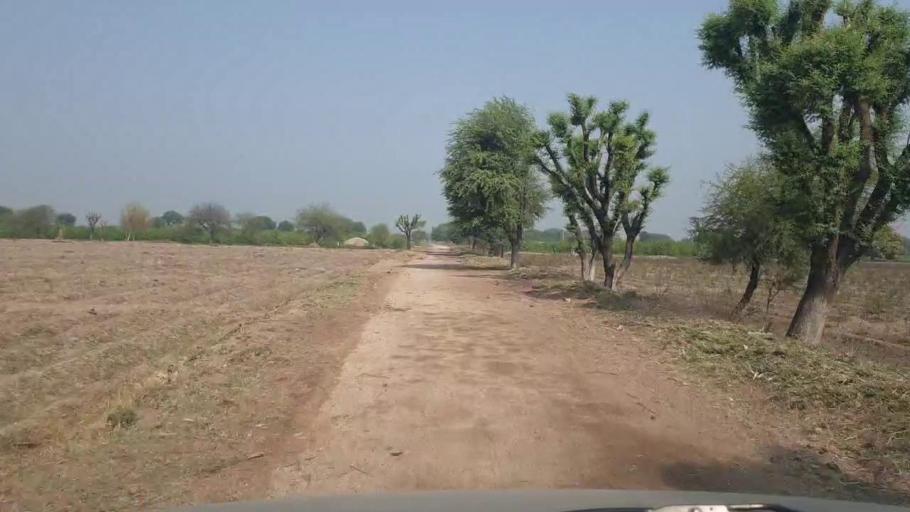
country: PK
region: Sindh
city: Umarkot
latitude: 25.3918
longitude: 69.7103
